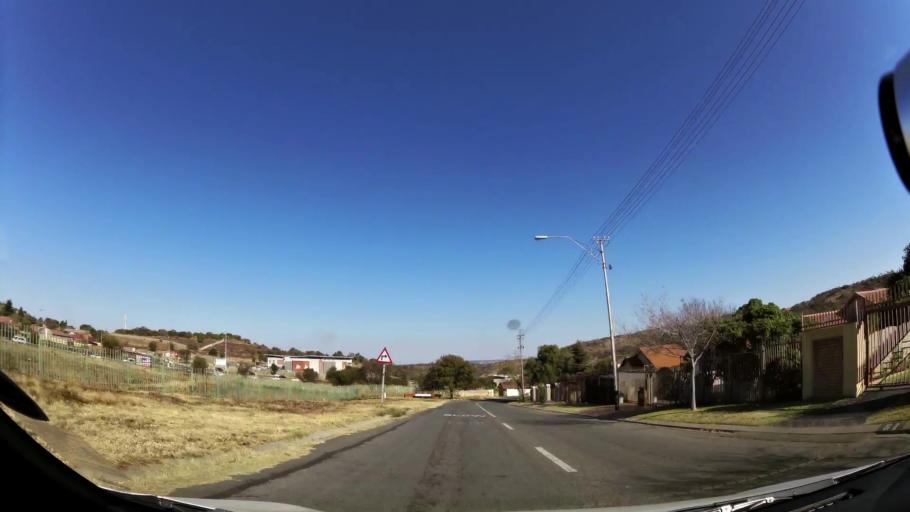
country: ZA
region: Gauteng
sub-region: City of Johannesburg Metropolitan Municipality
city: Johannesburg
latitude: -26.2765
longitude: 28.0335
